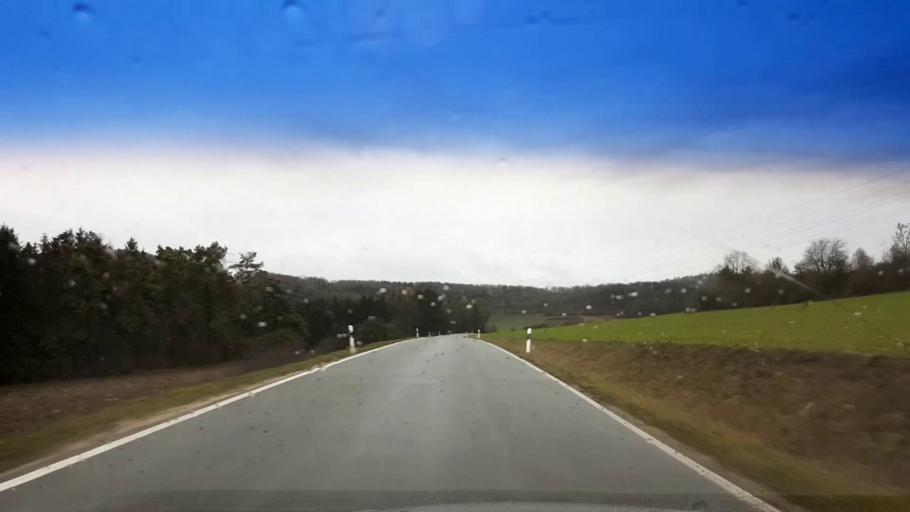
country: DE
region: Bavaria
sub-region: Upper Franconia
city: Poxdorf
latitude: 49.8827
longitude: 11.1094
